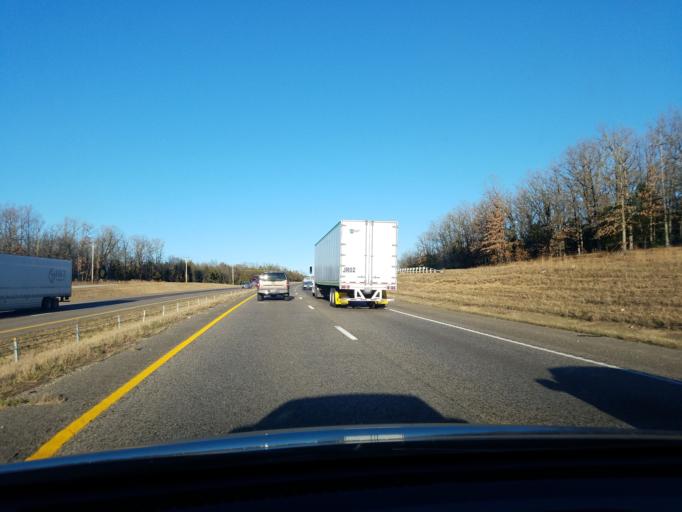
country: US
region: Missouri
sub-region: Franklin County
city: Sullivan
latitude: 38.2516
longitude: -91.1332
